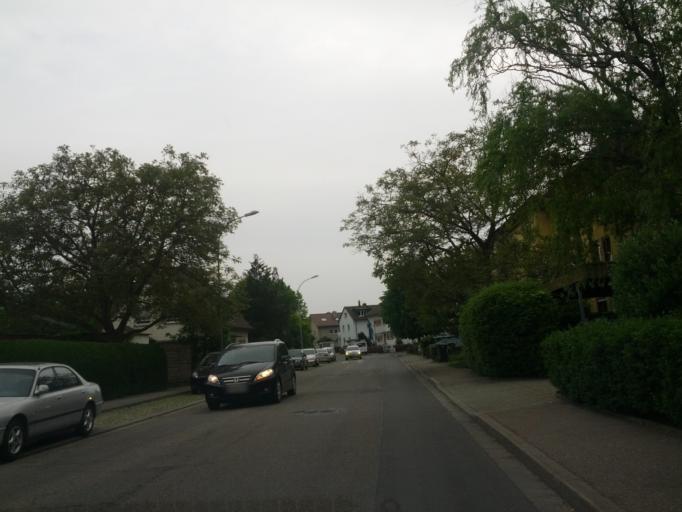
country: DE
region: Baden-Wuerttemberg
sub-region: Freiburg Region
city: Merzhausen
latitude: 47.9899
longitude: 7.8048
